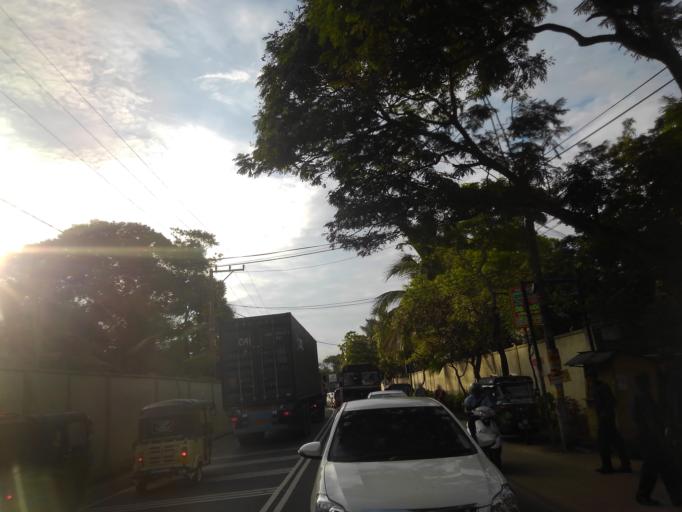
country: LK
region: Southern
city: Galle
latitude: 6.0375
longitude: 80.2276
